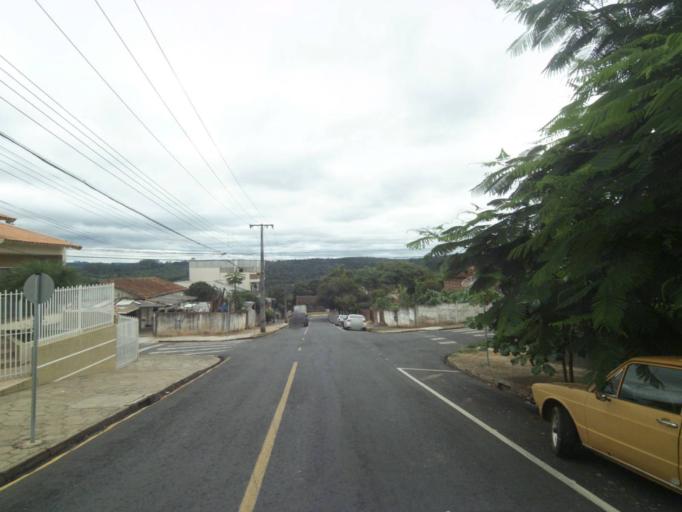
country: BR
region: Parana
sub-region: Telemaco Borba
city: Telemaco Borba
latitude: -24.3282
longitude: -50.6149
